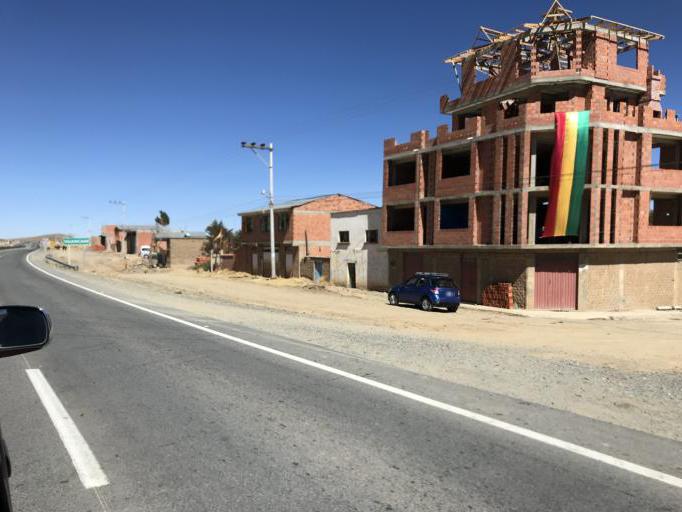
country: BO
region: La Paz
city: Batallas
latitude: -16.2582
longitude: -68.5623
